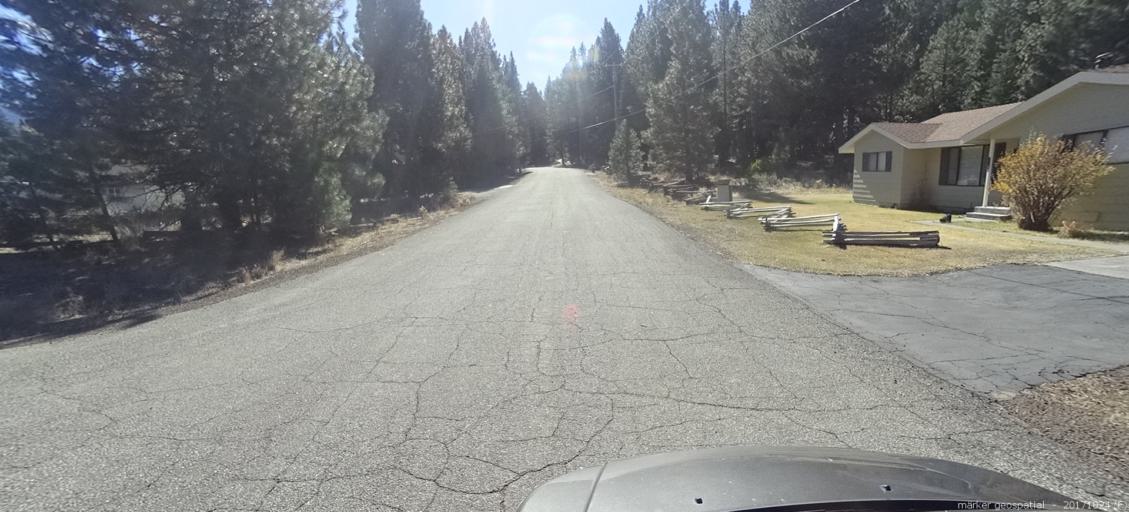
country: US
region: California
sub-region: Shasta County
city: Burney
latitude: 40.6556
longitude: -121.4648
